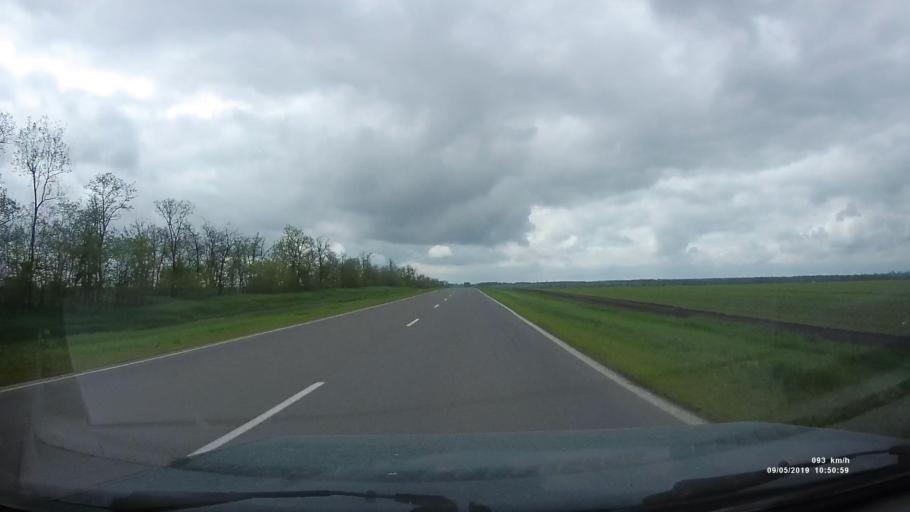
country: RU
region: Rostov
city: Peshkovo
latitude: 46.9211
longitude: 39.3553
